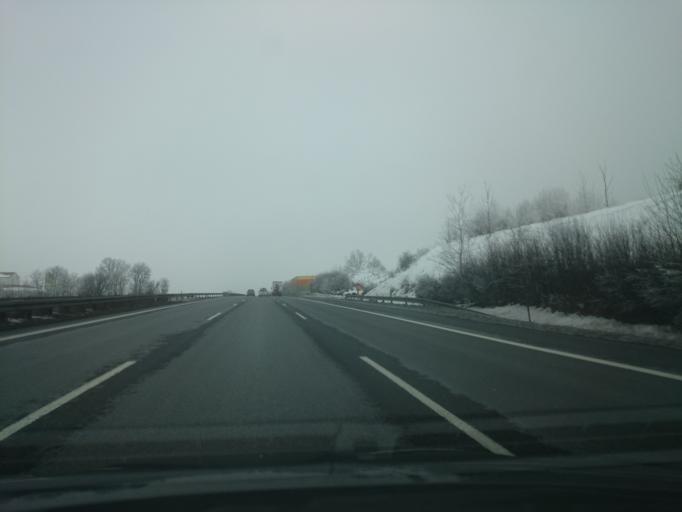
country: DE
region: Bavaria
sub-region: Upper Bavaria
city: Stammham
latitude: 48.8604
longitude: 11.4657
